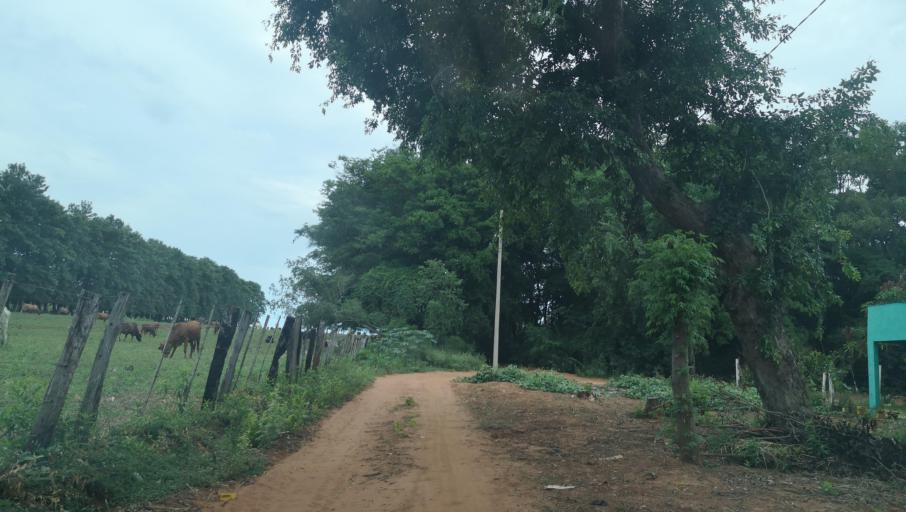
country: PY
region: San Pedro
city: Capiibary
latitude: -24.7364
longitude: -56.0192
